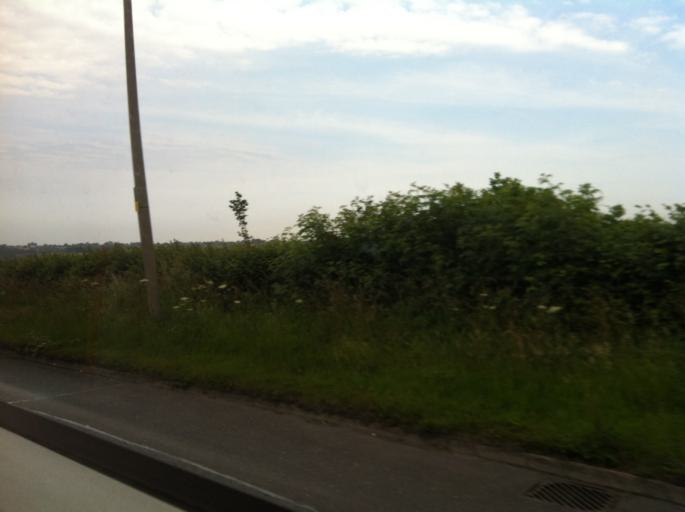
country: GB
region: Wales
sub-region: Vale of Glamorgan
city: Barry
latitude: 51.4060
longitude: -3.3105
